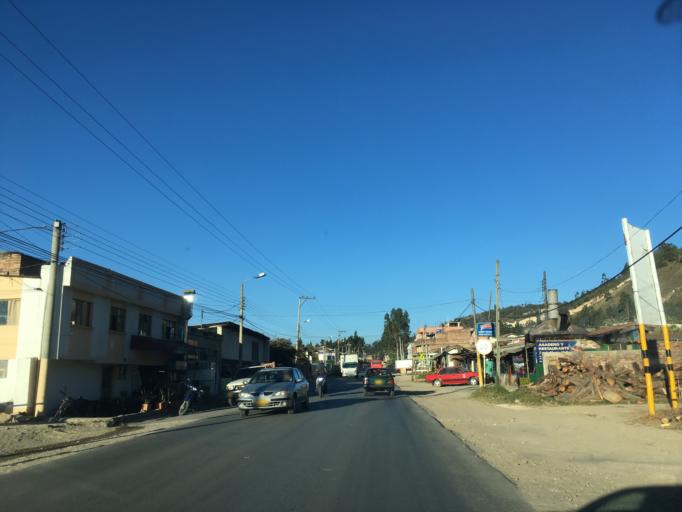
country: CO
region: Boyaca
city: Sogamoso
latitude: 5.6880
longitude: -72.9481
